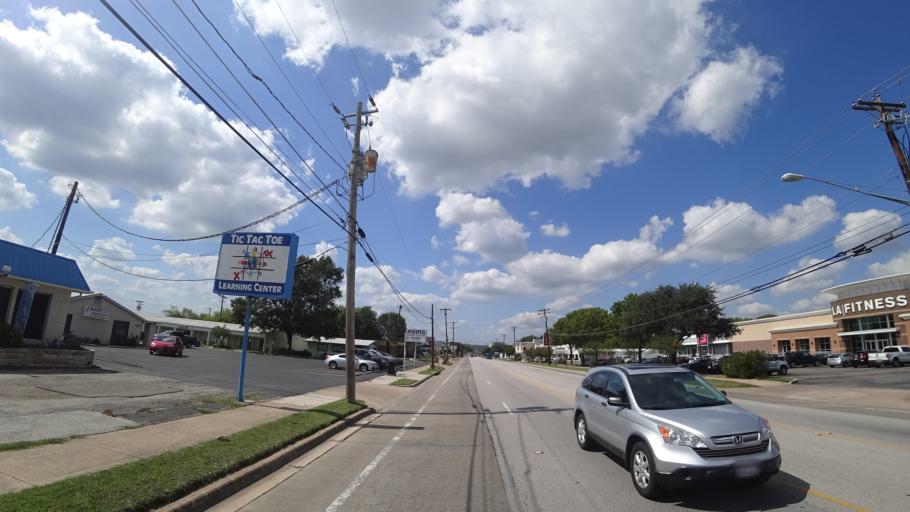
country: US
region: Texas
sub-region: Travis County
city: Austin
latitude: 30.3544
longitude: -97.7274
